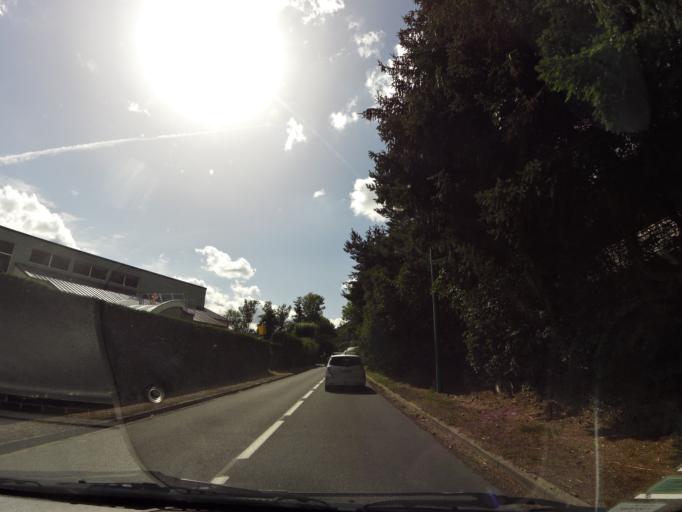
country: FR
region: Auvergne
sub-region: Departement du Puy-de-Dome
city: Mont-Dore
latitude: 45.5758
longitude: 2.9152
